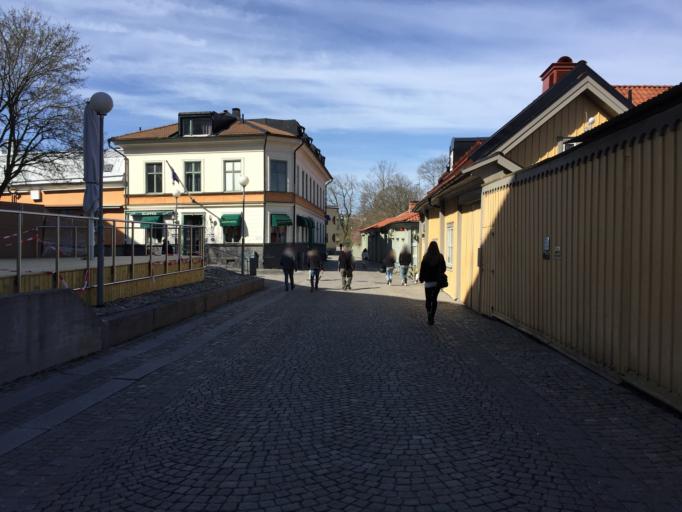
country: SE
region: Vaestmanland
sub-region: Vasteras
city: Vasteras
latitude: 59.6095
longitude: 16.5421
